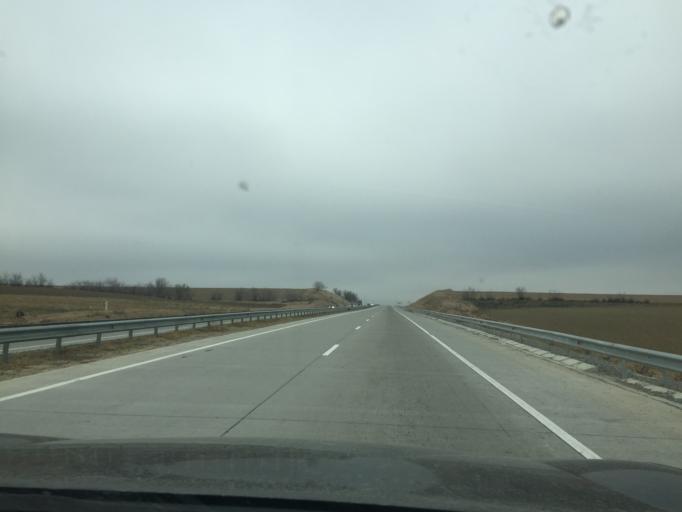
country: KZ
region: Ongtustik Qazaqstan
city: Aksu
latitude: 42.4753
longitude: 69.8904
